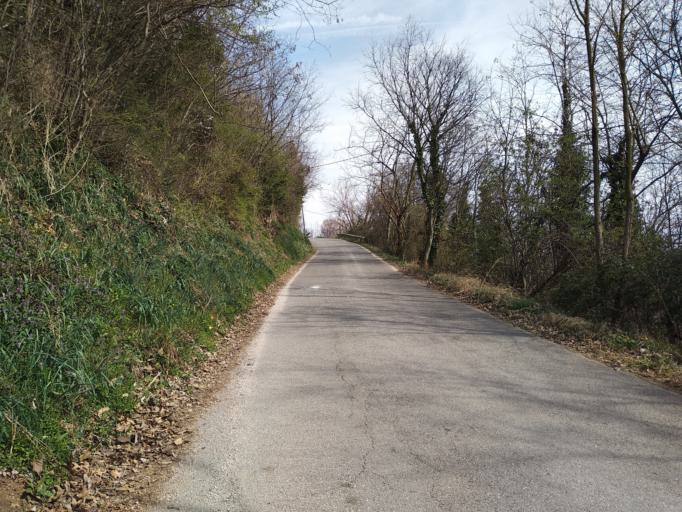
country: IT
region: Veneto
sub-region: Provincia di Vicenza
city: Barbarano Vicentino
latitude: 45.4120
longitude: 11.5431
